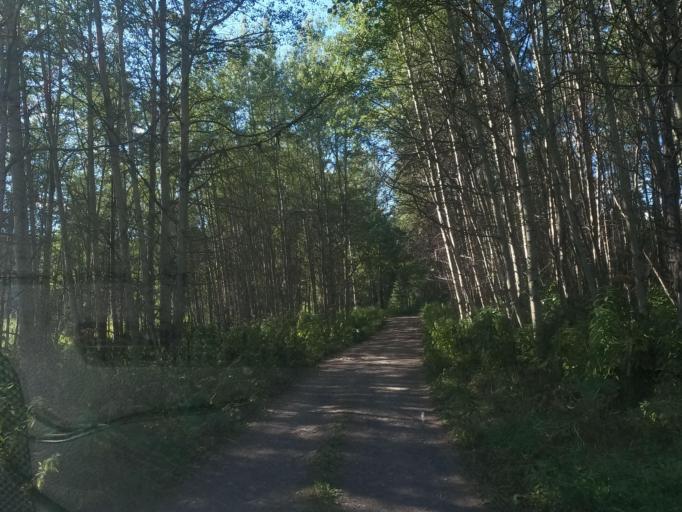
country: CA
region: British Columbia
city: Houston
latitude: 54.2861
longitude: -126.8538
